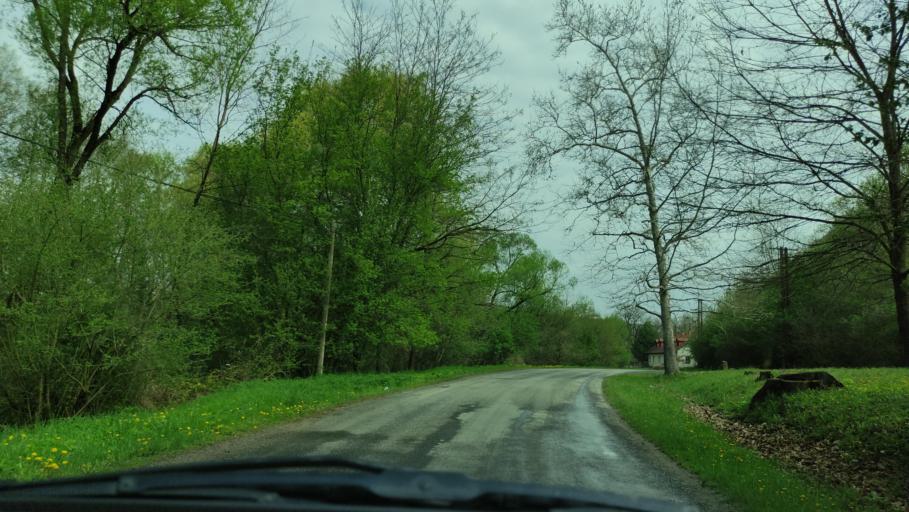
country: HU
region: Baranya
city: Magocs
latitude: 46.2689
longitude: 18.2156
